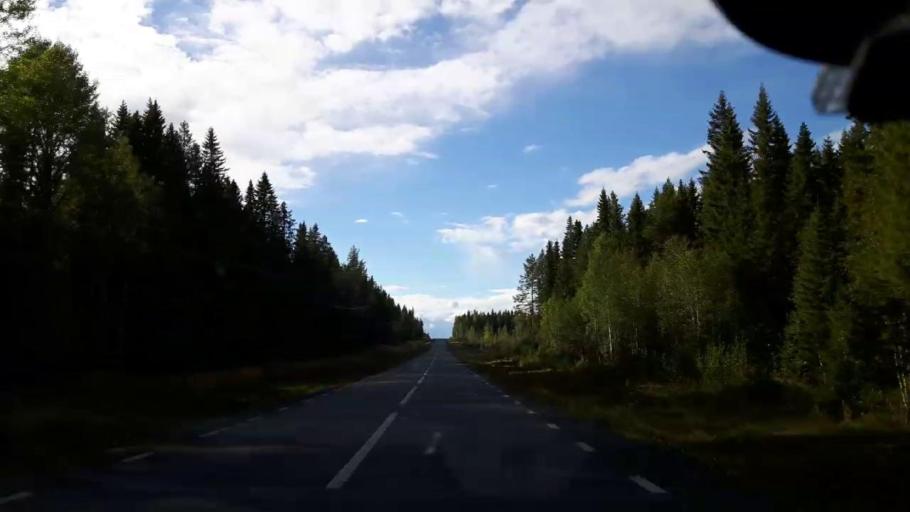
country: SE
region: Jaemtland
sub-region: Stroemsunds Kommun
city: Stroemsund
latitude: 63.5652
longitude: 15.7899
